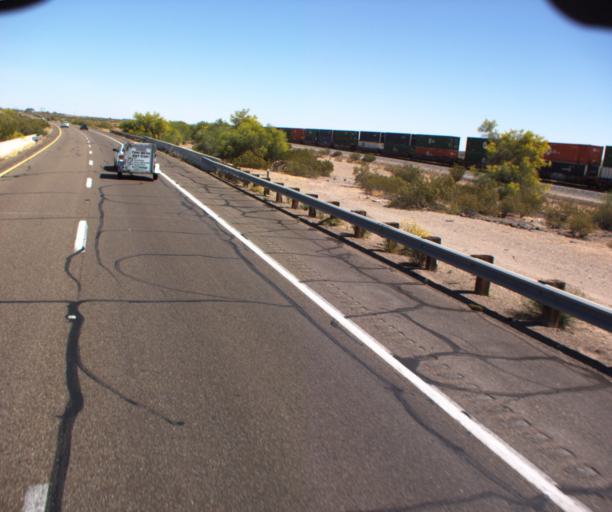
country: US
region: Arizona
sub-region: Maricopa County
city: Gila Bend
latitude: 32.8454
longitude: -113.2800
